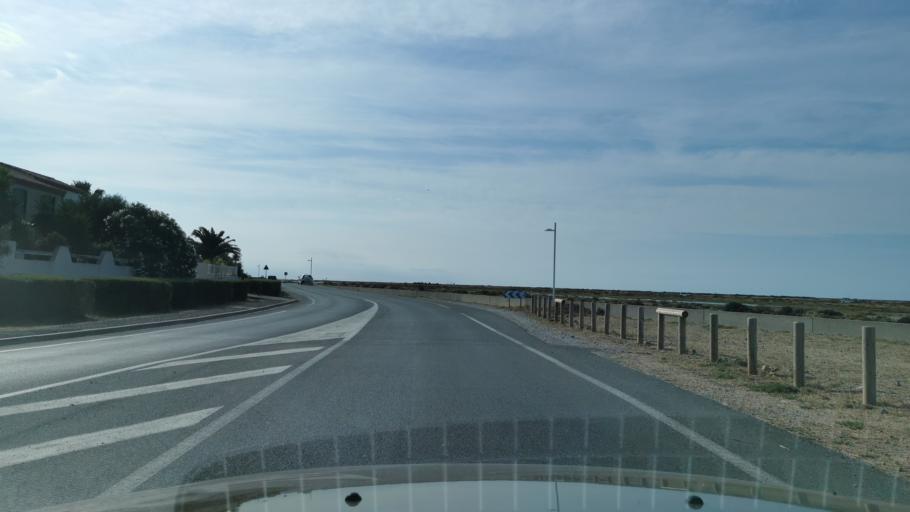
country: FR
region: Languedoc-Roussillon
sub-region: Departement de l'Aude
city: Gruissan
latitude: 43.1030
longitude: 3.0906
